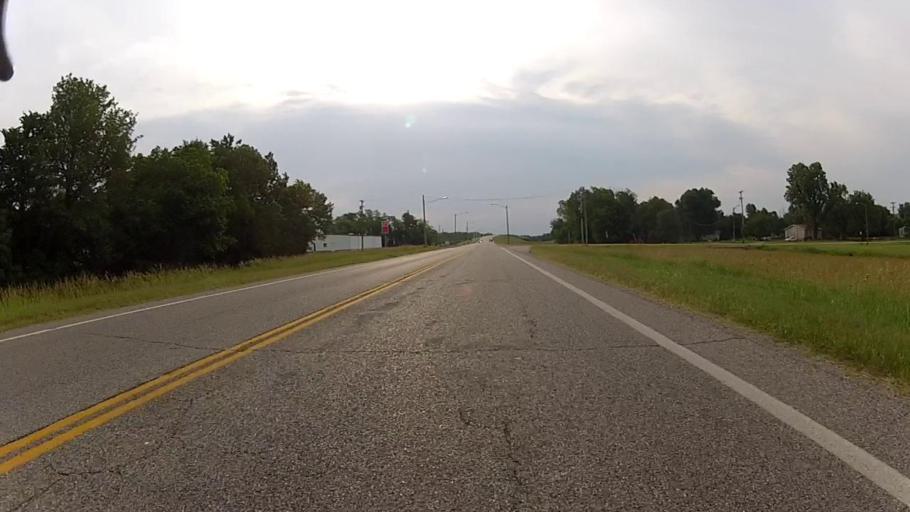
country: US
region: Kansas
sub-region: Cherokee County
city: Columbus
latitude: 37.1787
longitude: -94.8435
